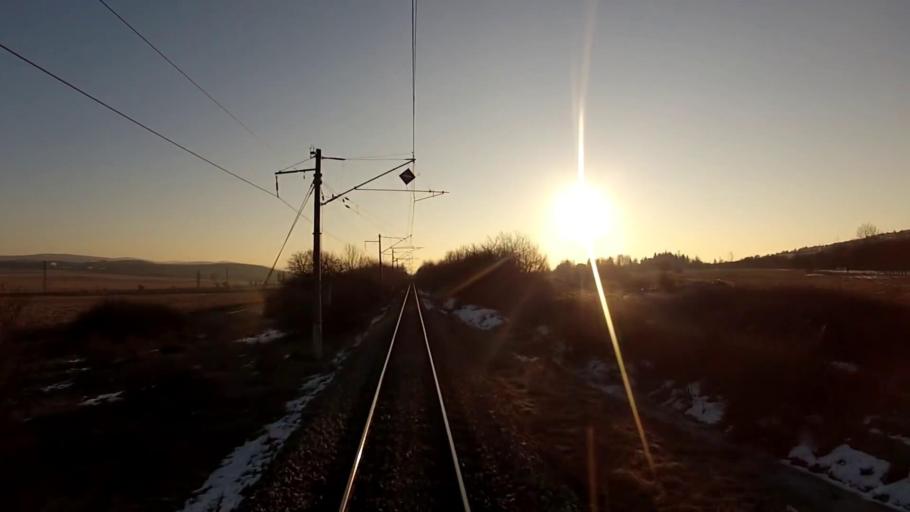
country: BG
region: Sofiya
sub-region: Obshtina Slivnitsa
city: Slivnitsa
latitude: 42.8755
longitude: 23.0158
